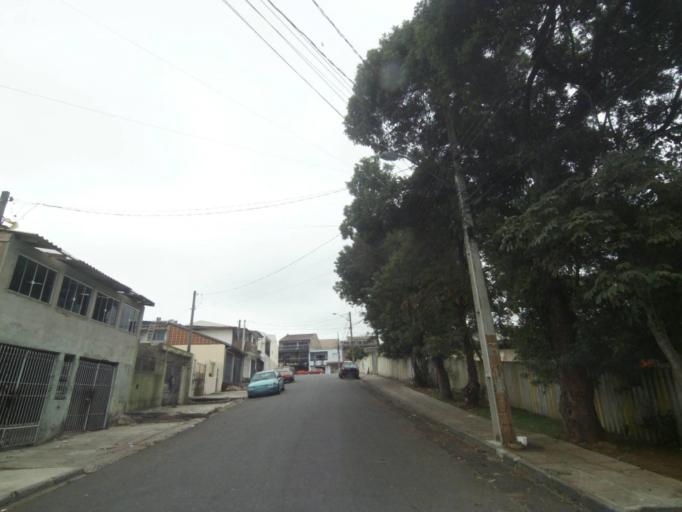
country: BR
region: Parana
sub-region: Curitiba
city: Curitiba
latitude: -25.4988
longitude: -49.3445
